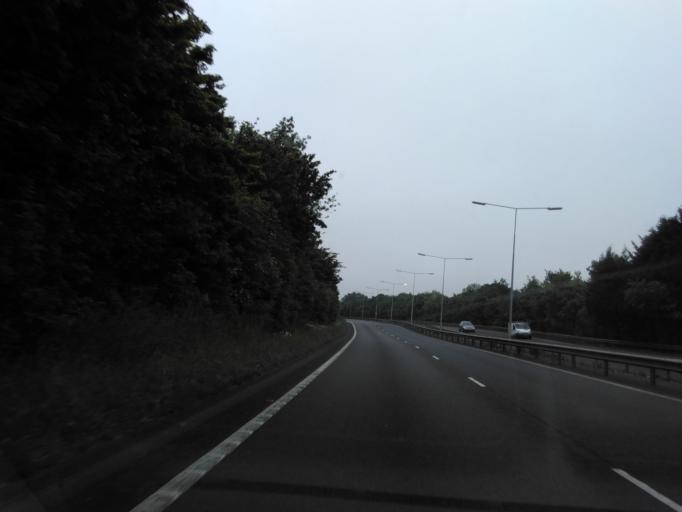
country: GB
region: England
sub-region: Kent
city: Dunkirk
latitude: 51.3131
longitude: 0.9507
